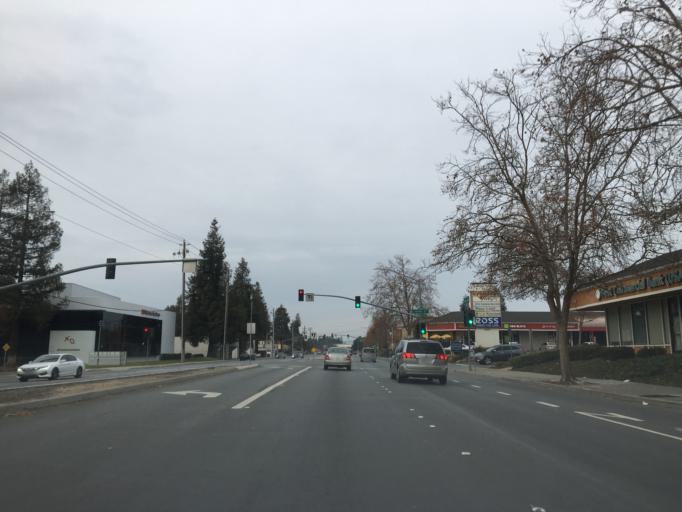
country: US
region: California
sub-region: Santa Clara County
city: Milpitas
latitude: 37.4909
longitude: -121.9300
